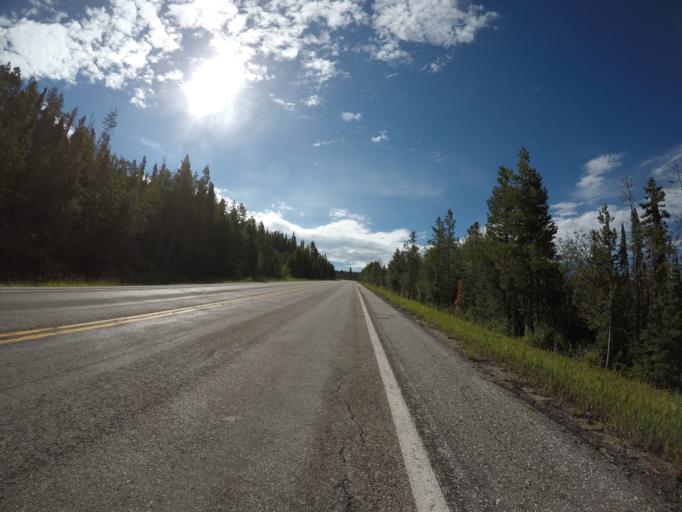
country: US
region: Wyoming
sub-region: Carbon County
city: Saratoga
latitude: 41.3284
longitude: -106.4747
